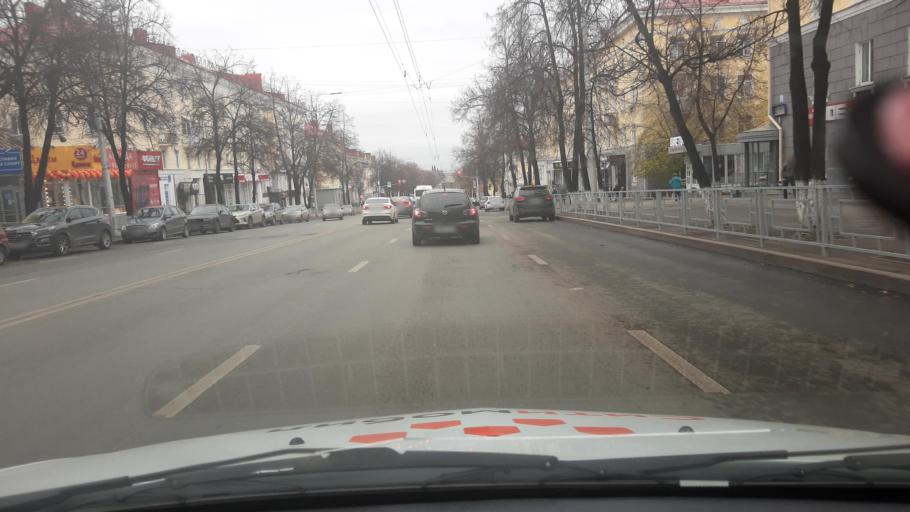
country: RU
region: Bashkortostan
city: Ufa
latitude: 54.8168
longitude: 56.0774
